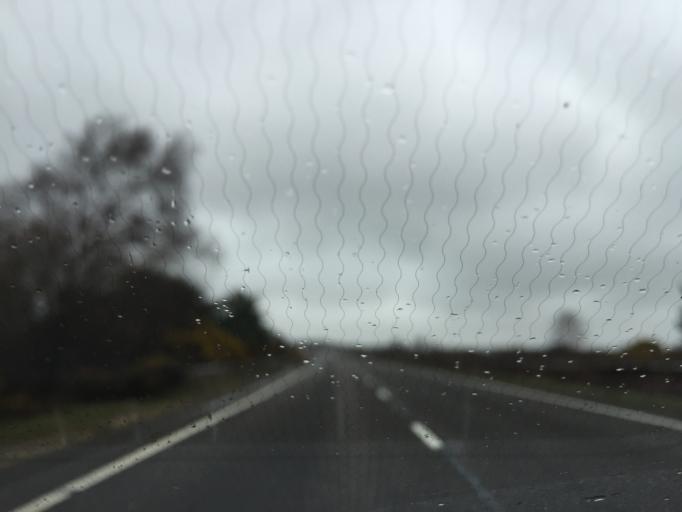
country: GB
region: England
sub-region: Hampshire
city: Bransgore
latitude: 50.8725
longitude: -1.6951
